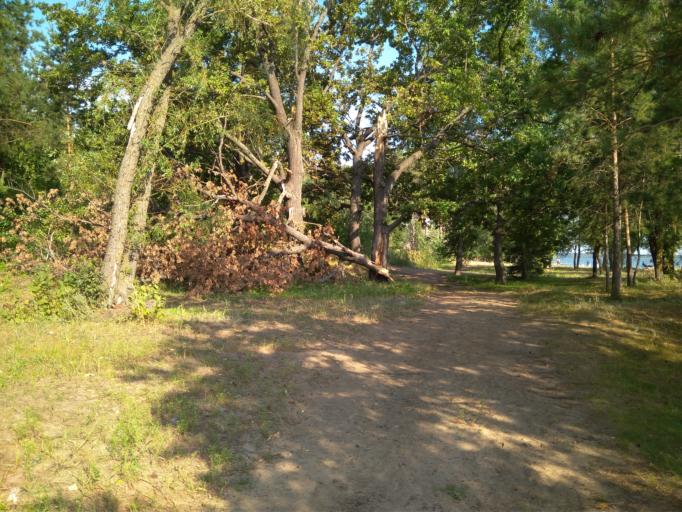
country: RU
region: Ulyanovsk
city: Staraya Mayna
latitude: 54.6222
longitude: 48.9598
